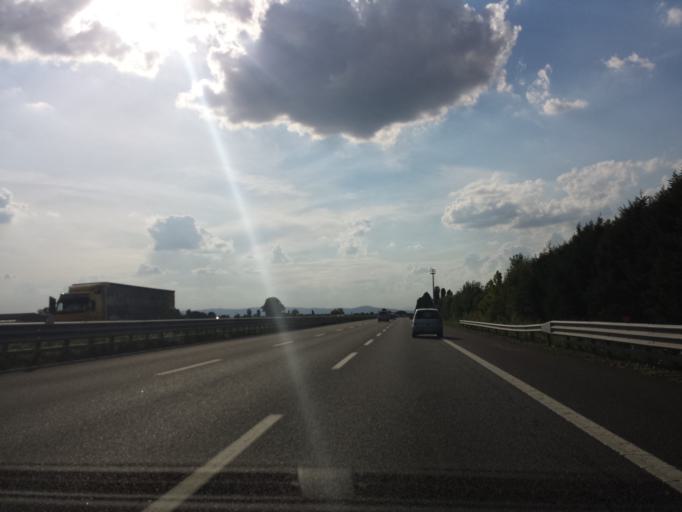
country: IT
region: Veneto
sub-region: Provincia di Padova
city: Taggi
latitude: 45.4542
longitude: 11.8059
